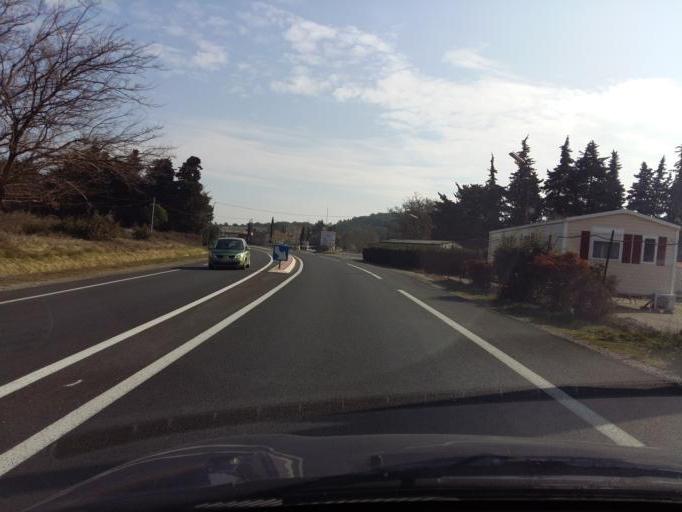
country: FR
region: Provence-Alpes-Cote d'Azur
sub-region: Departement des Bouches-du-Rhone
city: Orgon
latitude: 43.7944
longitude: 5.0175
